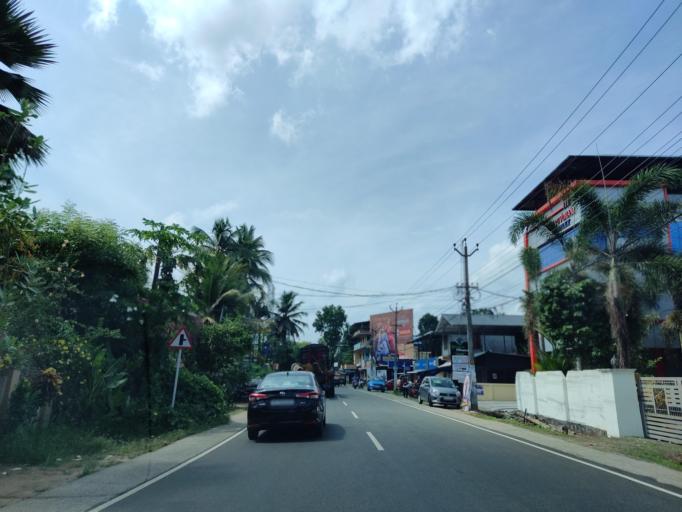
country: IN
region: Kerala
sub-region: Alappuzha
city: Mavelikara
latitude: 9.2897
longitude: 76.5324
